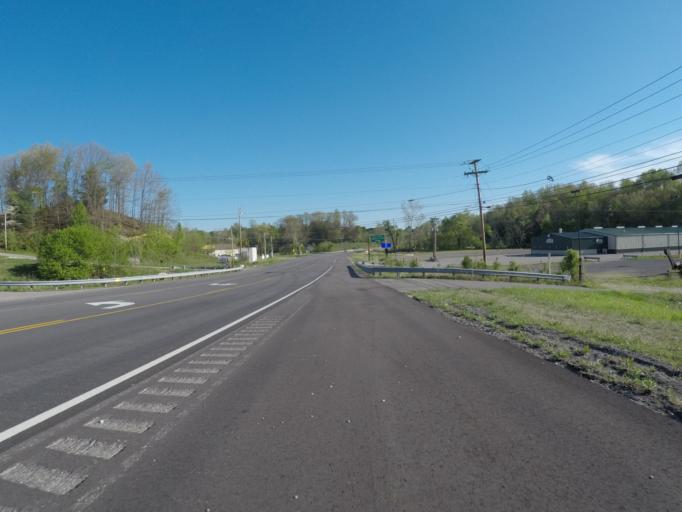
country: US
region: Kentucky
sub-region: Boyd County
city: Meads
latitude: 38.3586
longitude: -82.6975
